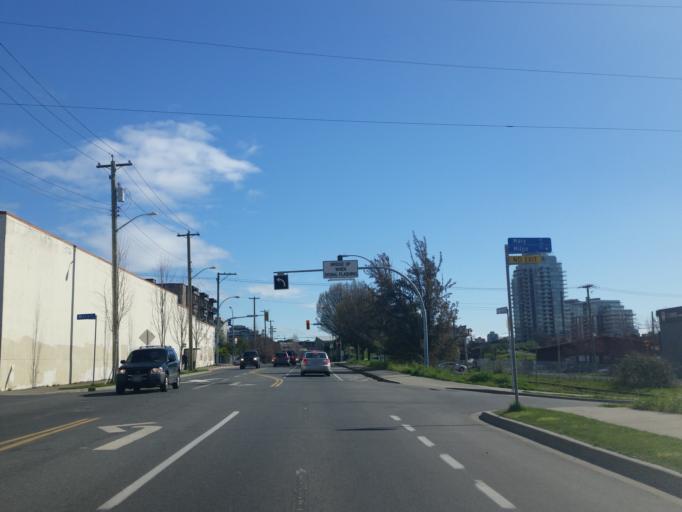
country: CA
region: British Columbia
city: Victoria
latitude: 48.4304
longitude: -123.3863
